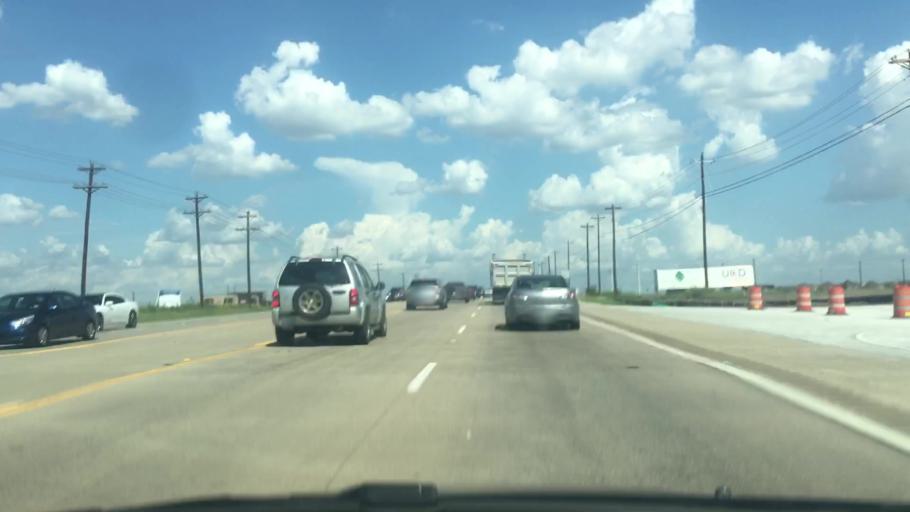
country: US
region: Texas
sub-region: Denton County
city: Little Elm
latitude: 33.2190
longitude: -96.8847
